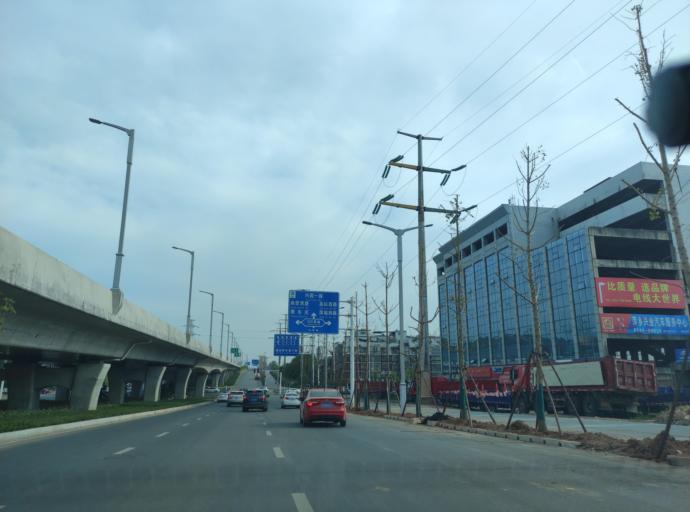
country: CN
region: Jiangxi Sheng
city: Pingxiang
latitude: 27.6606
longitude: 113.8245
